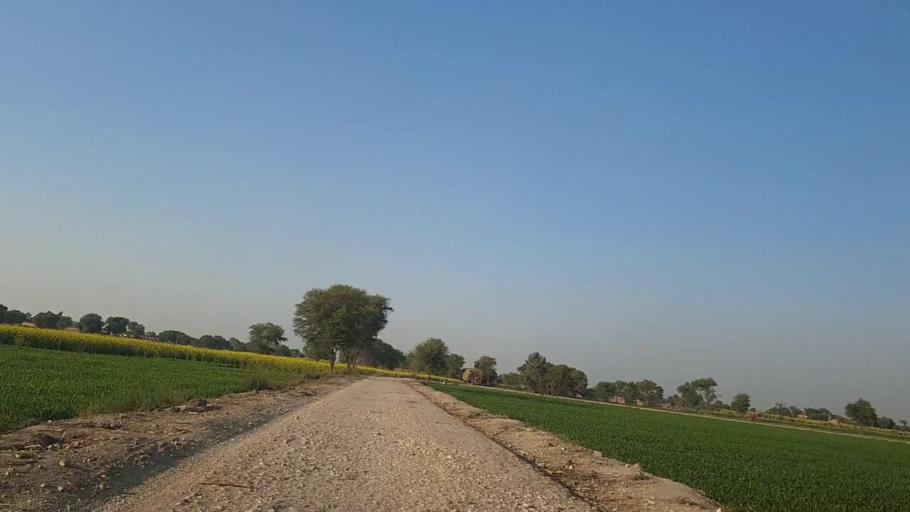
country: PK
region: Sindh
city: Sakrand
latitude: 26.3019
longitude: 68.1268
